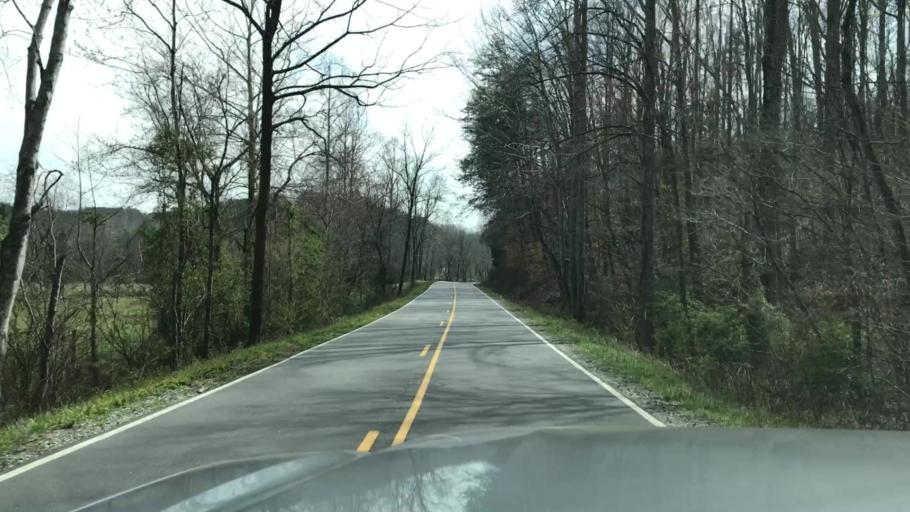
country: US
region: North Carolina
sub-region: Rutherford County
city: Spindale
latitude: 35.4502
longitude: -81.8817
